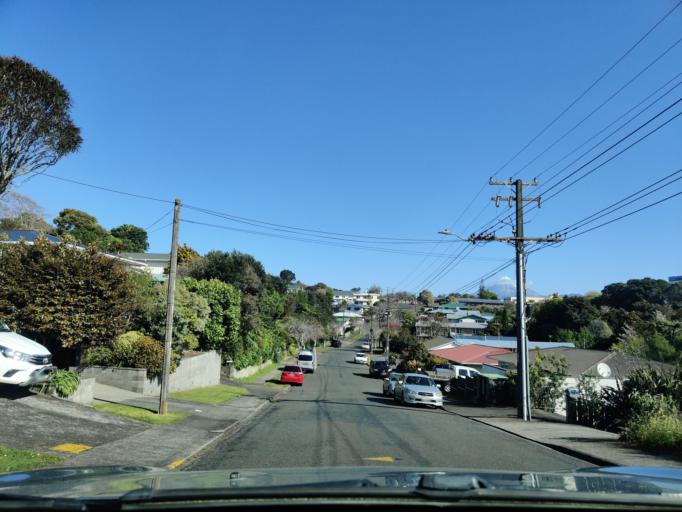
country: NZ
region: Taranaki
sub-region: New Plymouth District
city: New Plymouth
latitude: -39.0683
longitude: 174.0562
